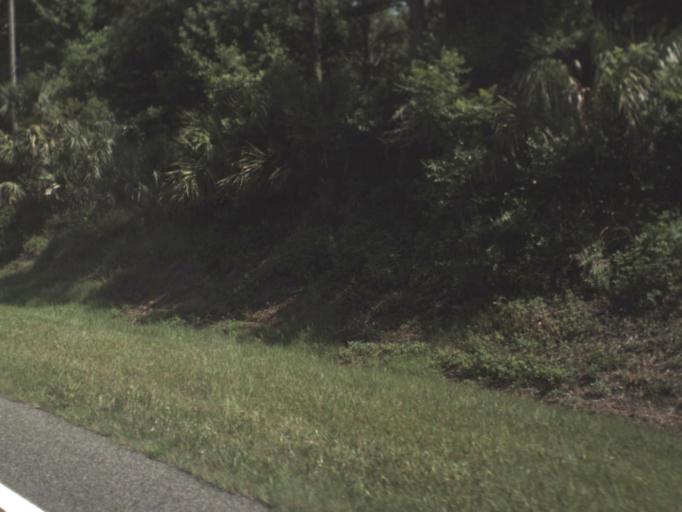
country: US
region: Florida
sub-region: Marion County
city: Citra
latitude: 29.4866
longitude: -82.2472
